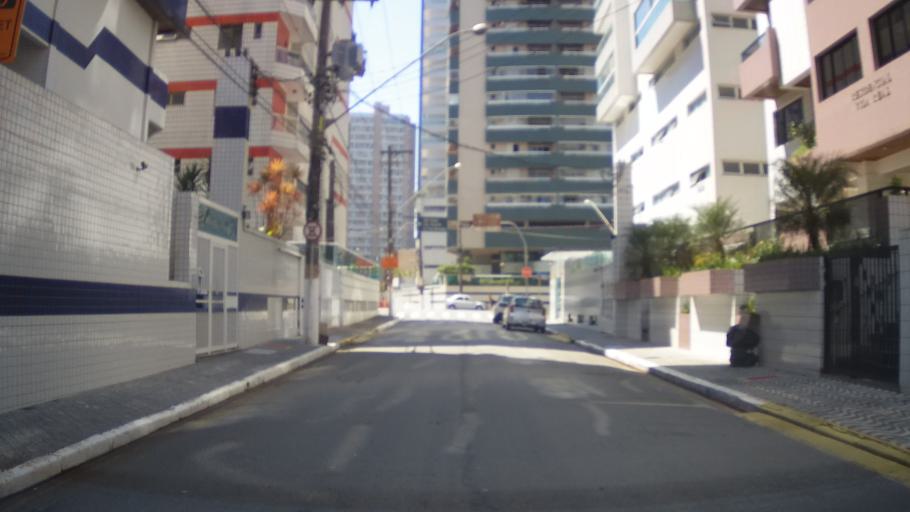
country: BR
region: Sao Paulo
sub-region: Praia Grande
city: Praia Grande
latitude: -24.0159
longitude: -46.3995
